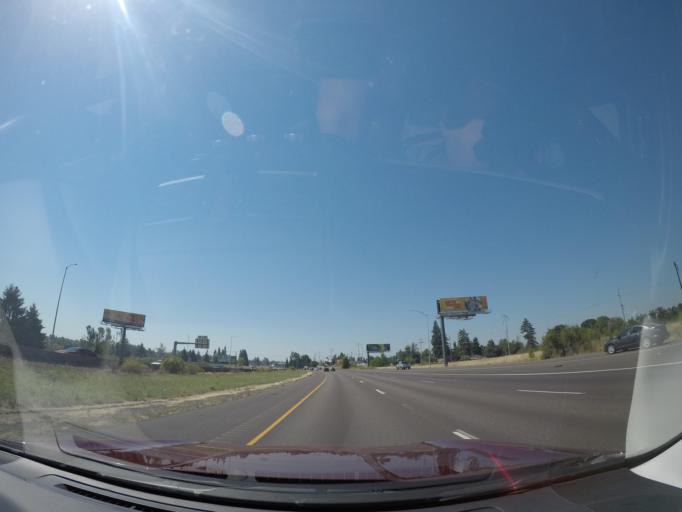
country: US
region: Oregon
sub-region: Marion County
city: Hayesville
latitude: 44.9990
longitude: -123.0005
